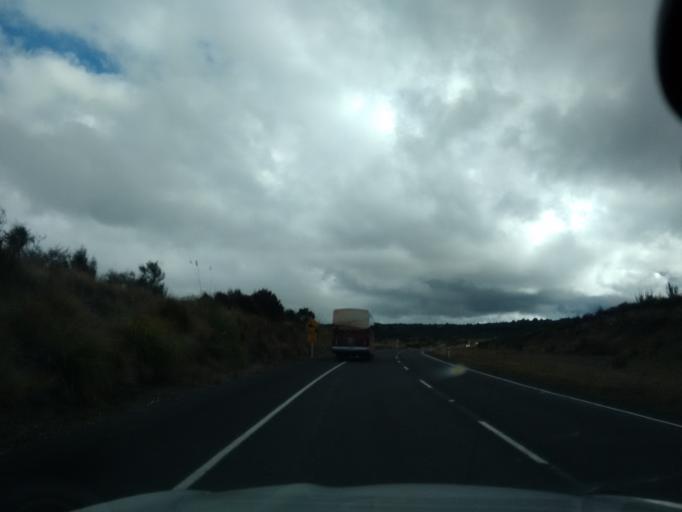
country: NZ
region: Waikato
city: Turangi
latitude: -39.0655
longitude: 175.5738
